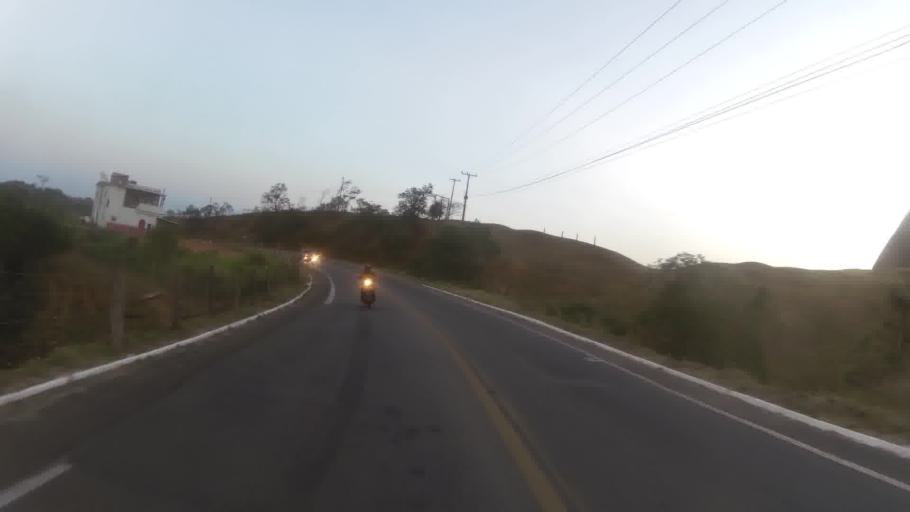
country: BR
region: Espirito Santo
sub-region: Piuma
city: Piuma
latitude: -20.8699
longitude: -40.7632
